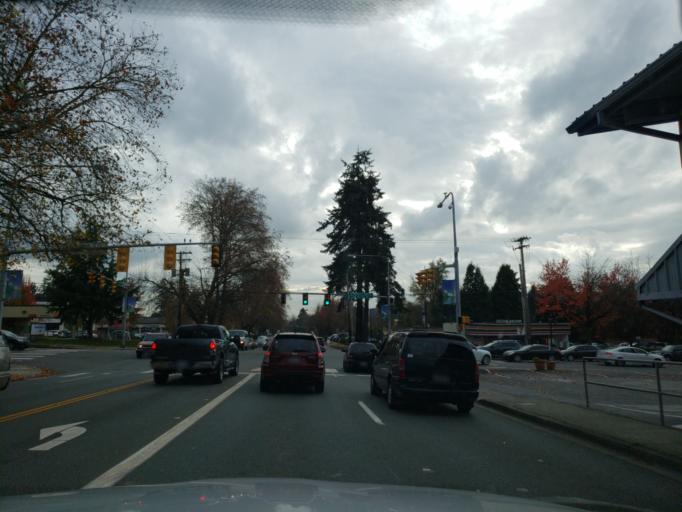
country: US
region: Washington
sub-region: King County
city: Woodinville
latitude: 47.7550
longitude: -122.1528
